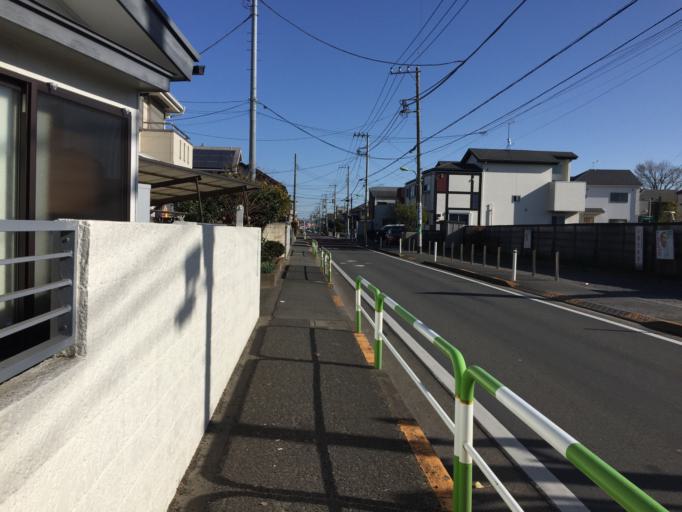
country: JP
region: Tokyo
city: Chofugaoka
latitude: 35.6233
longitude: 139.6037
